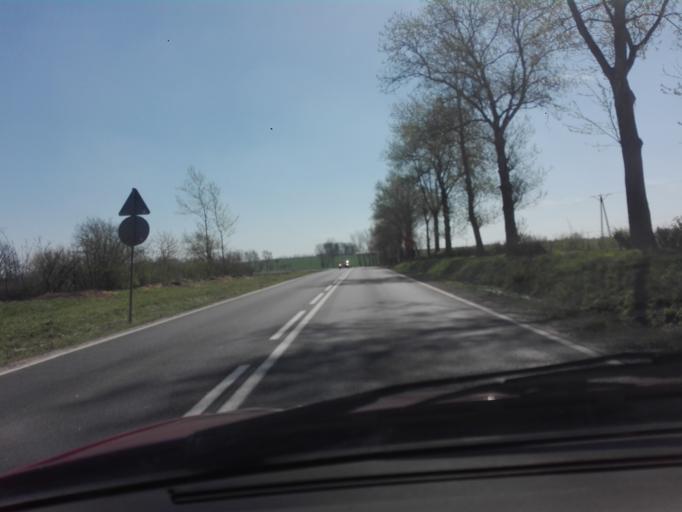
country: PL
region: West Pomeranian Voivodeship
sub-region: Koszalin
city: Koszalin
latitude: 54.1476
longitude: 16.2468
